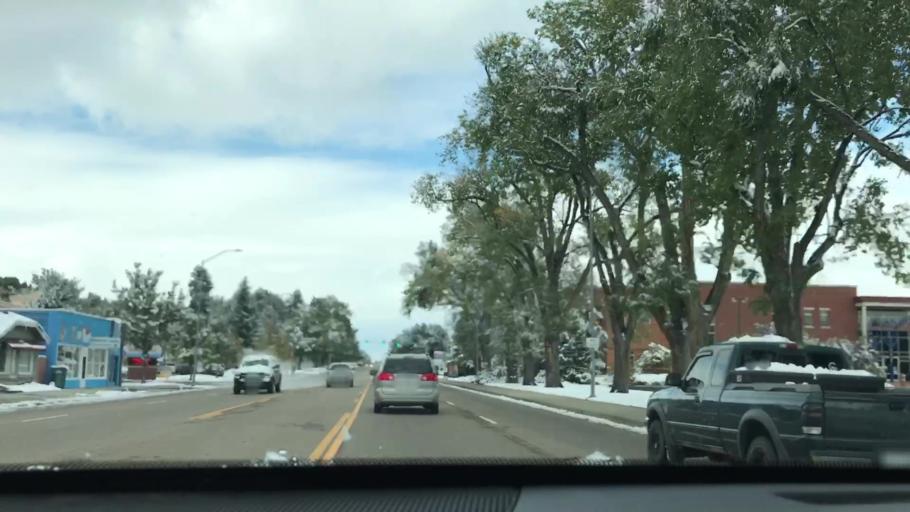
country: US
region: Colorado
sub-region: Boulder County
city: Longmont
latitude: 40.1762
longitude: -105.1024
